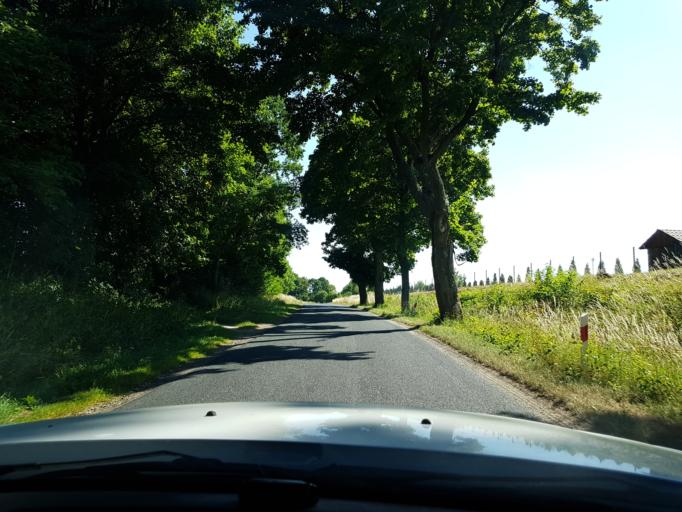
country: PL
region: West Pomeranian Voivodeship
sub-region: Powiat swidwinski
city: Slawoborze
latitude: 53.9109
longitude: 15.7734
